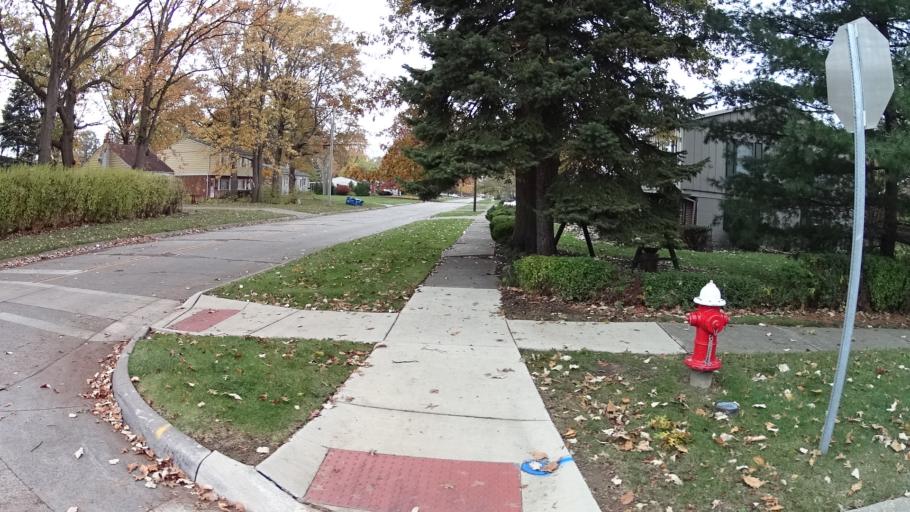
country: US
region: Ohio
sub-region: Lorain County
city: Sheffield Lake
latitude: 41.4696
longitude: -82.1410
